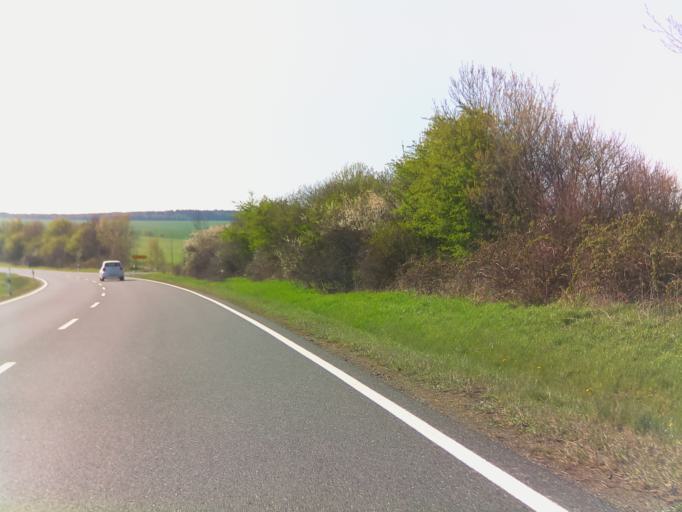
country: DE
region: Thuringia
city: Tanna
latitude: 50.5382
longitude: 11.8622
